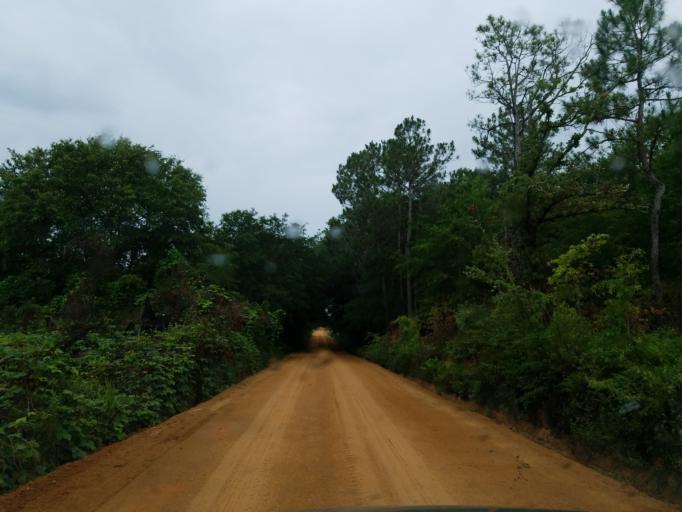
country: US
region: Georgia
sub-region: Crisp County
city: Cordele
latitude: 32.0008
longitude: -83.6975
